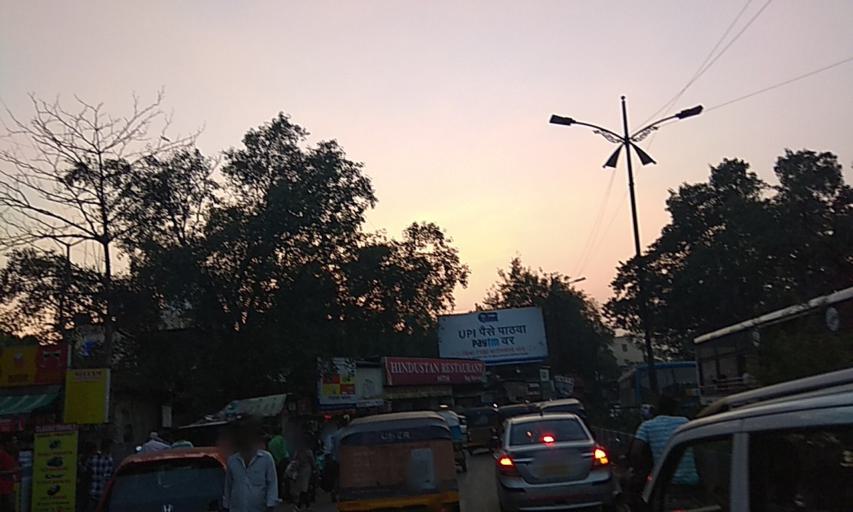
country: IN
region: Maharashtra
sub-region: Pune Division
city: Pune
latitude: 18.5279
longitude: 73.8755
